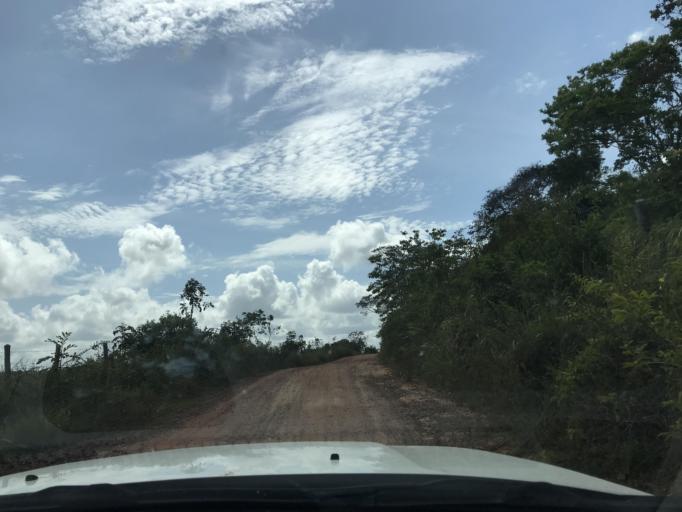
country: BR
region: Bahia
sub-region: Entre Rios
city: Entre Rios
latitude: -12.1789
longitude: -38.0610
